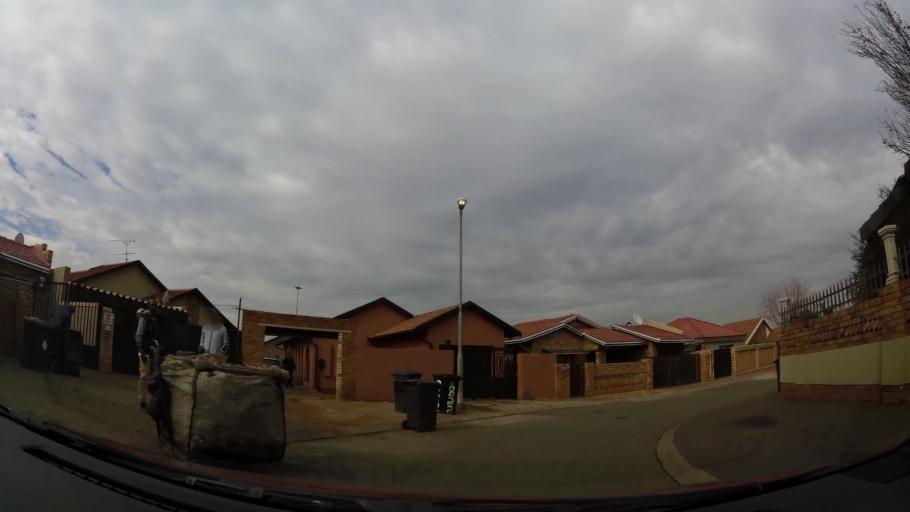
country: ZA
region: Gauteng
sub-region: City of Johannesburg Metropolitan Municipality
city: Soweto
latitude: -26.2740
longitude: 27.8306
